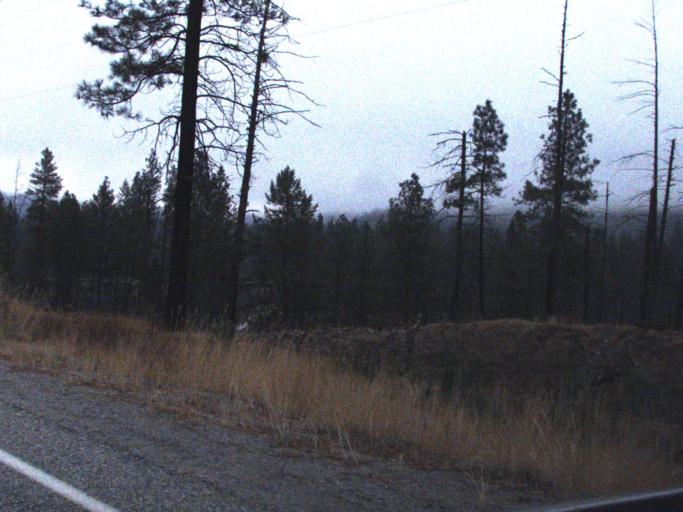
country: US
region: Washington
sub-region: Stevens County
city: Kettle Falls
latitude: 48.7557
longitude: -118.1348
